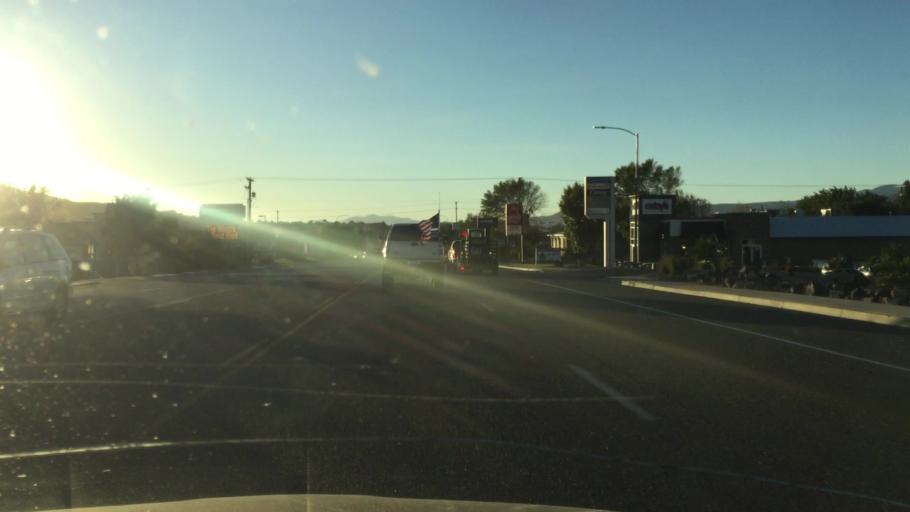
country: US
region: Utah
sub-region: Washington County
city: Hurricane
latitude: 37.1762
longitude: -113.3067
